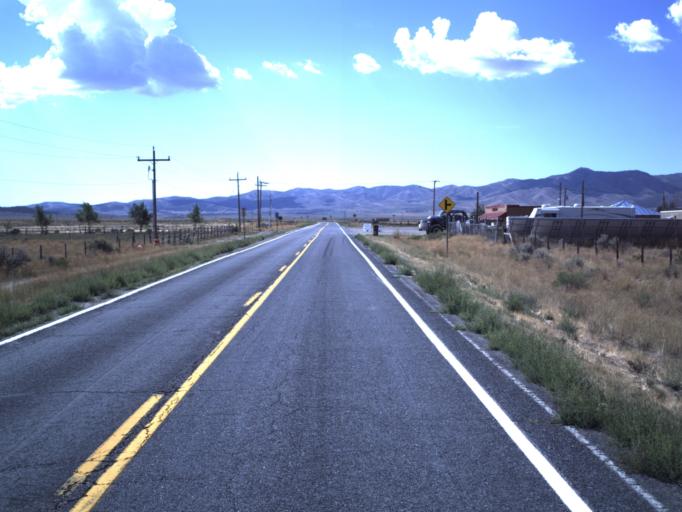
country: US
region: Utah
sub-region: Tooele County
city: Tooele
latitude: 40.0940
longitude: -112.4309
